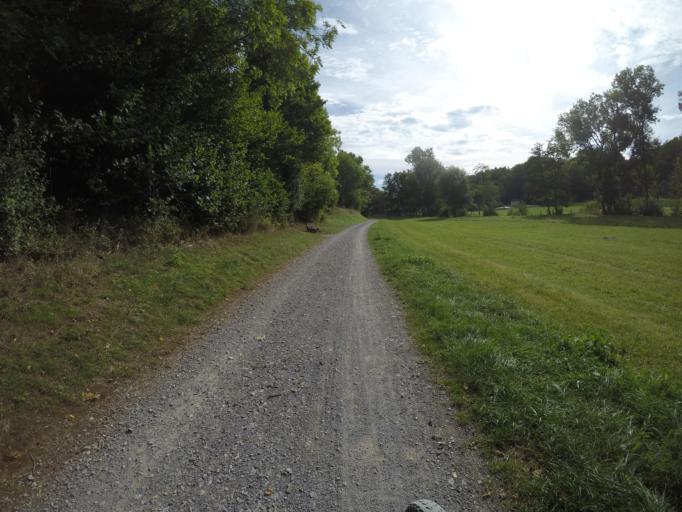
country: DE
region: Baden-Wuerttemberg
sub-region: Regierungsbezirk Stuttgart
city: Eberdingen
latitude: 48.8864
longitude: 8.9641
